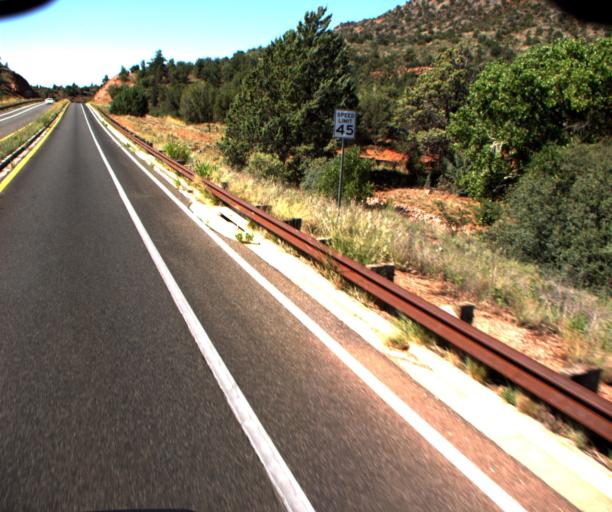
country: US
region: Arizona
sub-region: Yavapai County
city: Big Park
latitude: 34.7658
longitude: -111.7659
